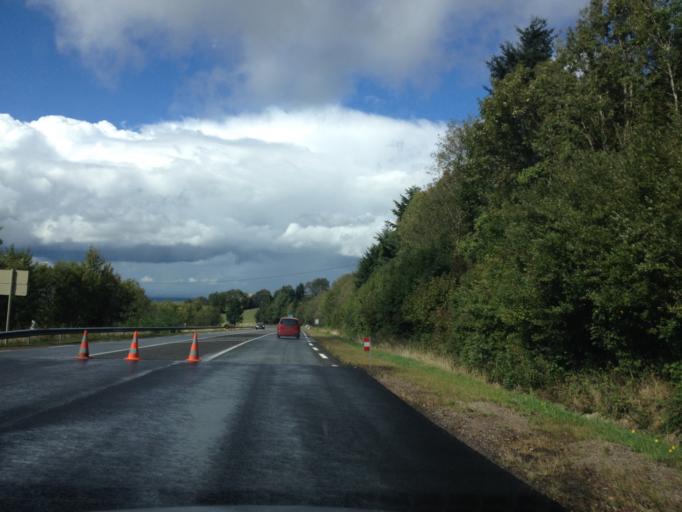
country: FR
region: Rhone-Alpes
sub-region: Departement du Rhone
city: Amplepuis
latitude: 45.9190
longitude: 4.3220
